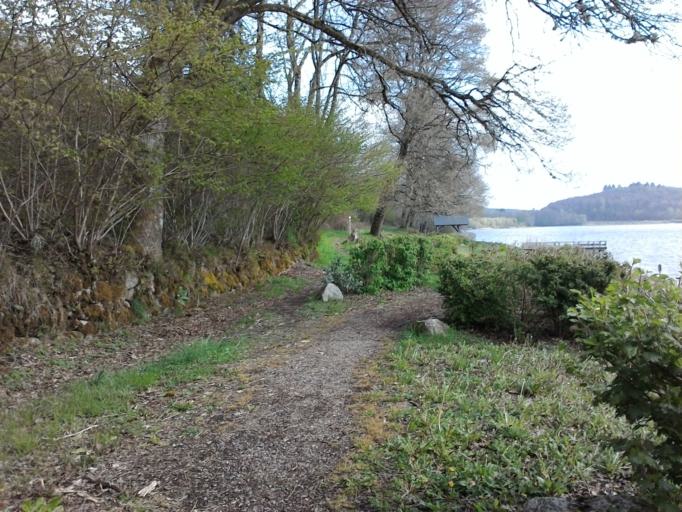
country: FR
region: Bourgogne
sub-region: Departement de la Cote-d'Or
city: Saulieu
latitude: 47.2460
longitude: 4.1874
